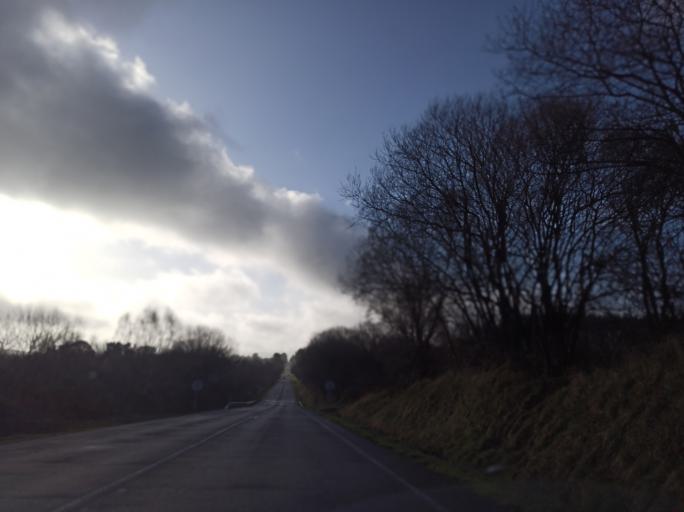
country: ES
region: Galicia
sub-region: Provincia da Coruna
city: Curtis
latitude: 43.0977
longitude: -8.0201
